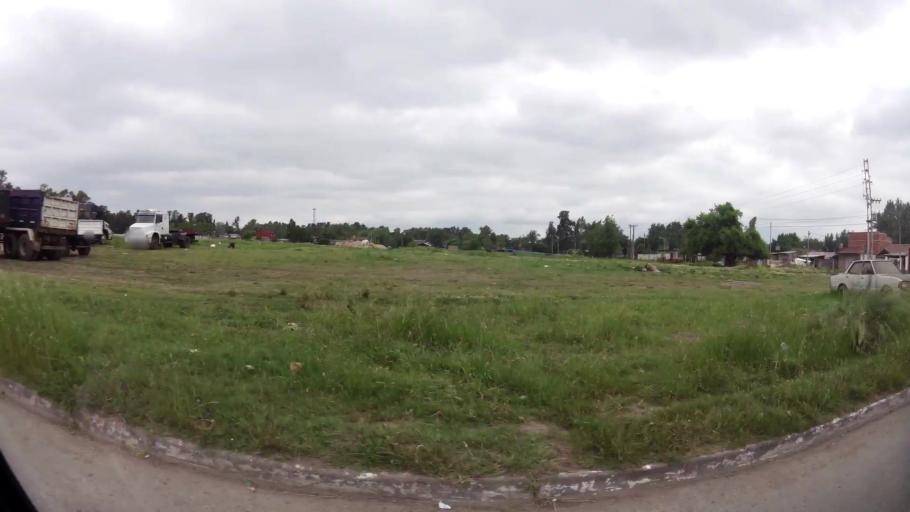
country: AR
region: Buenos Aires
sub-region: Partido de Ezeiza
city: Ezeiza
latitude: -34.8673
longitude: -58.5091
